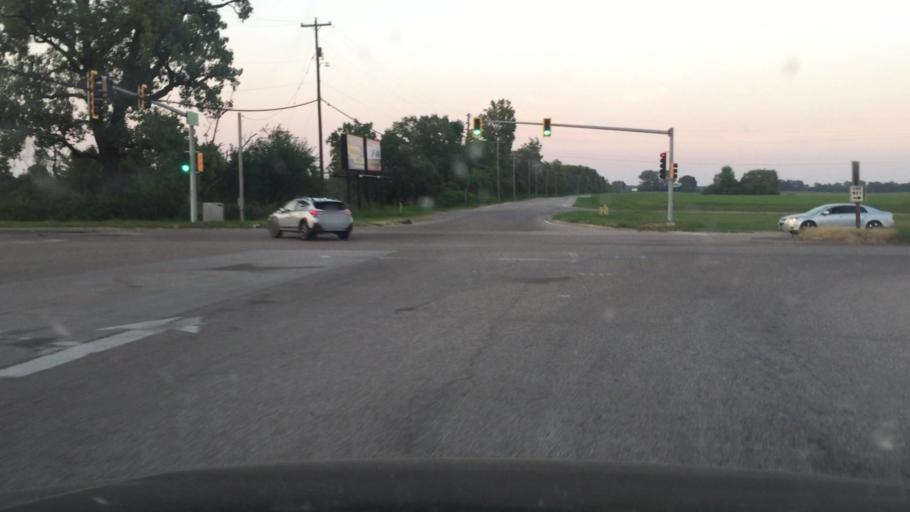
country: US
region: Illinois
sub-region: Madison County
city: Madison
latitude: 38.6642
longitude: -90.1428
